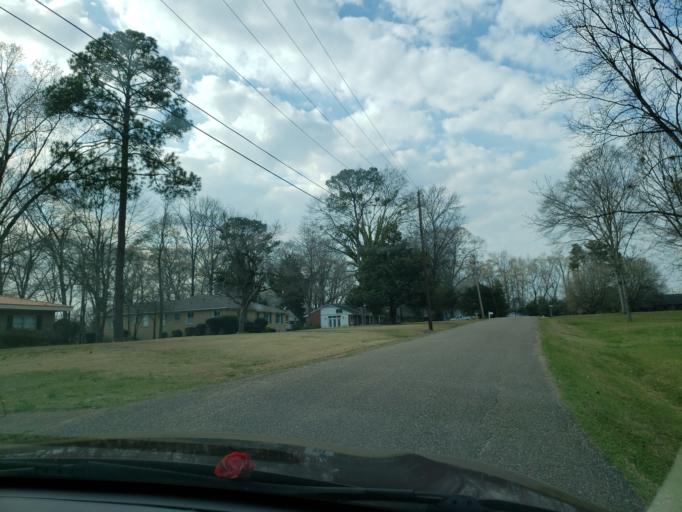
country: US
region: Alabama
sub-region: Hale County
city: Greensboro
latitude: 32.6968
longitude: -87.5949
